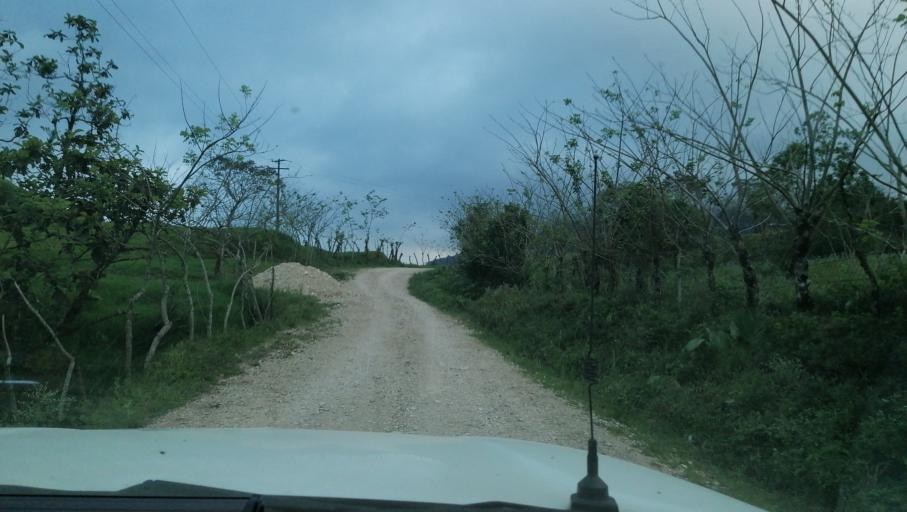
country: MX
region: Chiapas
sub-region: Francisco Leon
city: San Miguel la Sardina
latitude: 17.2882
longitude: -93.2699
